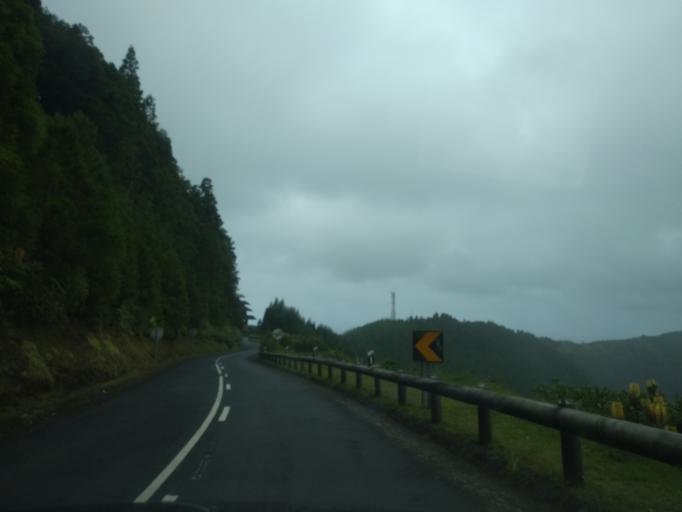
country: PT
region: Azores
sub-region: Ponta Delgada
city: Arrifes
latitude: 37.8393
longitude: -25.7916
